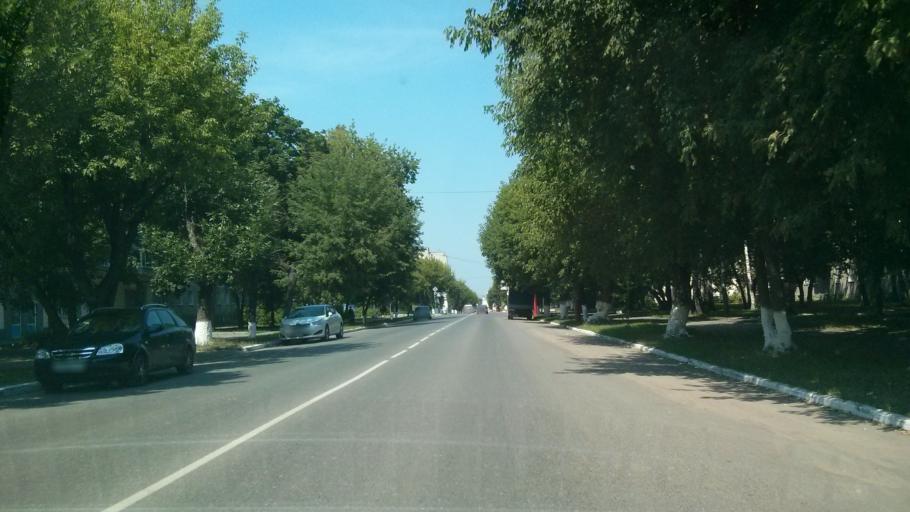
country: RU
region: Vladimir
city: Murom
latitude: 55.5708
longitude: 42.0537
